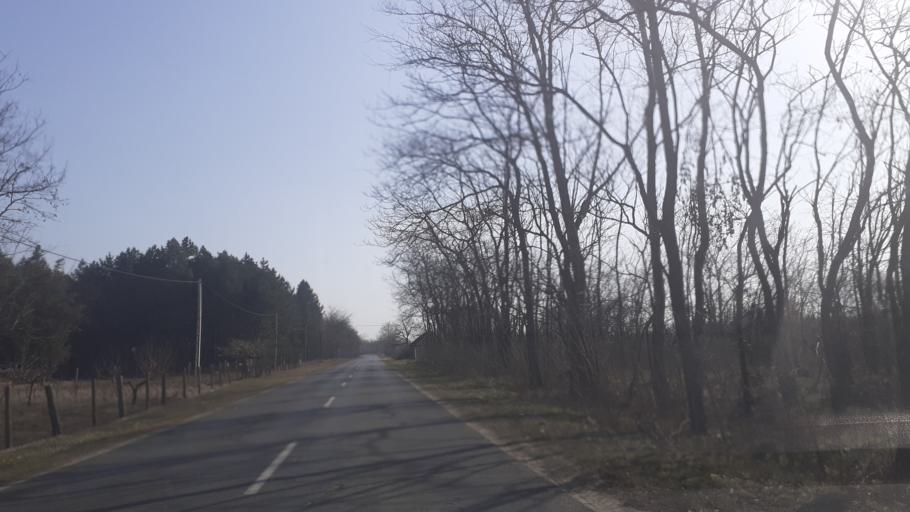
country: HU
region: Bacs-Kiskun
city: Lajosmizse
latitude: 46.9858
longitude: 19.5601
